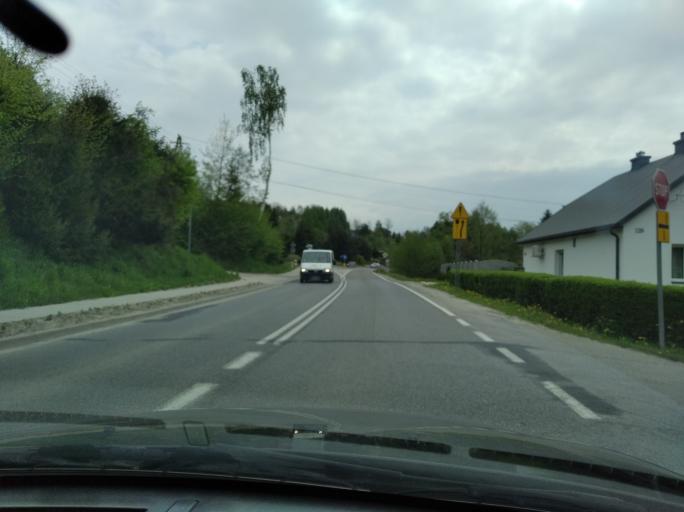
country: PL
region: Lesser Poland Voivodeship
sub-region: Powiat tarnowski
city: Tarnowiec
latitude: 49.9558
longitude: 21.0031
